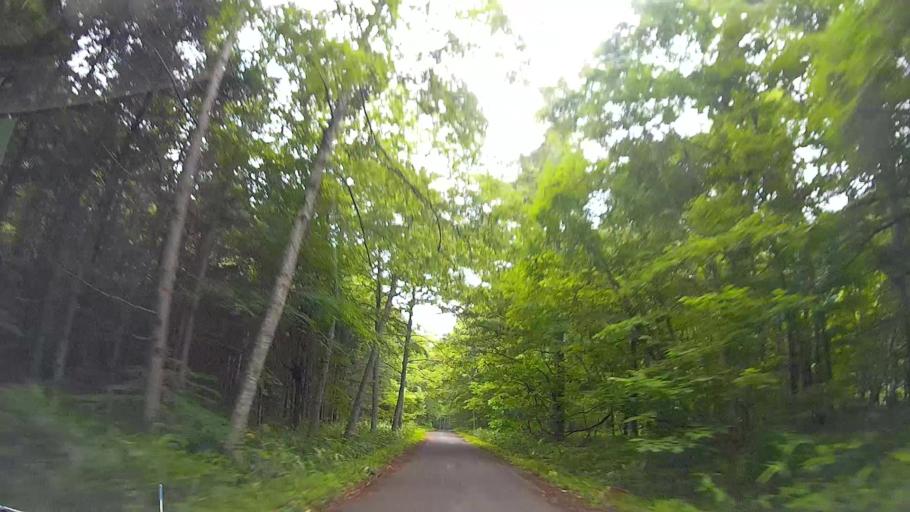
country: JP
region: Hokkaido
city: Nanae
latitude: 42.0532
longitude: 140.4961
